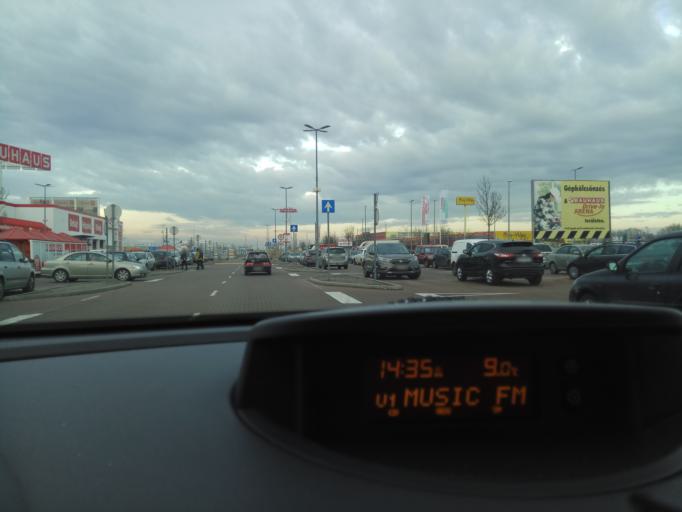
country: HU
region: Pest
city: Dunakeszi
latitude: 47.6090
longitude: 19.1145
